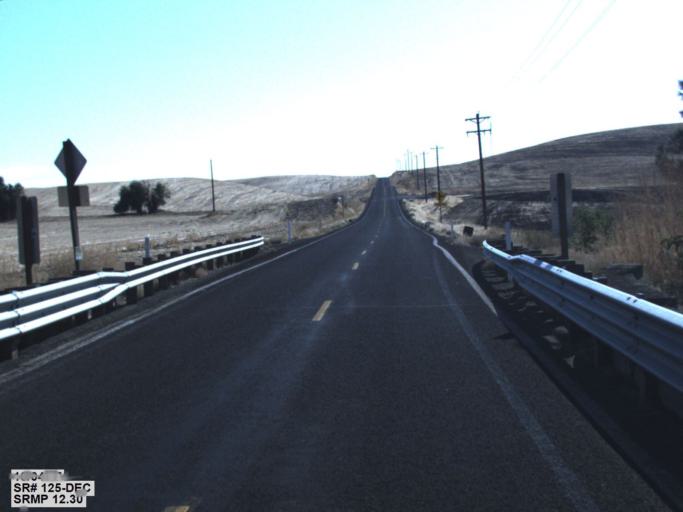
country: US
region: Washington
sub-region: Walla Walla County
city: Walla Walla
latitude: 46.1497
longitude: -118.3726
